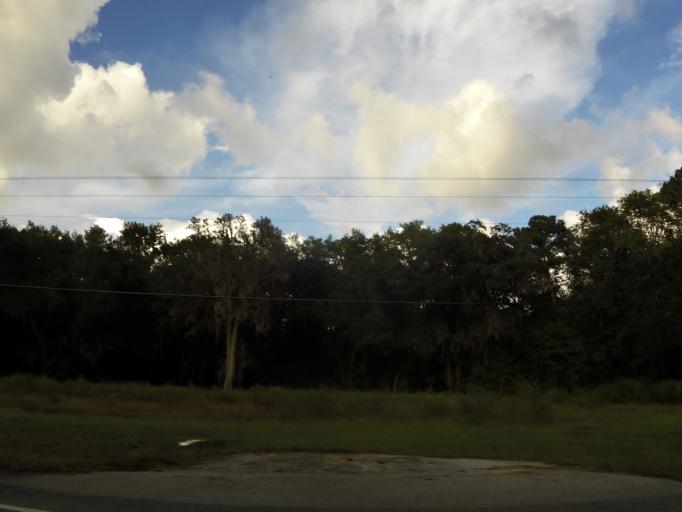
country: US
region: Georgia
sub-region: Liberty County
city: Midway
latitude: 31.7232
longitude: -81.4202
